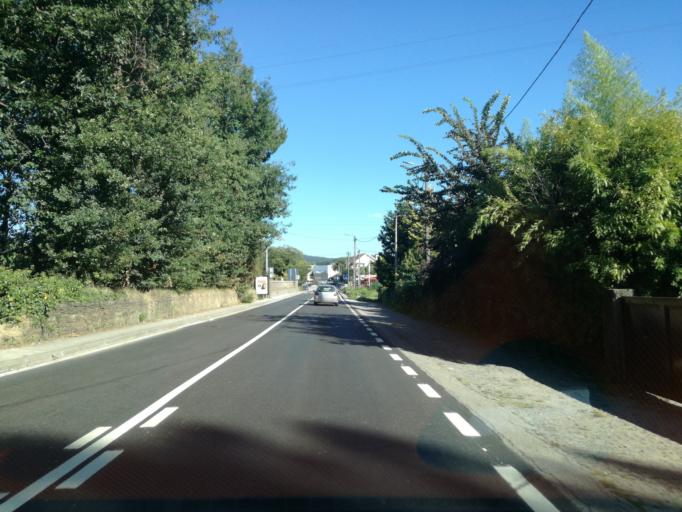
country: PT
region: Porto
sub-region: Valongo
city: Alfena
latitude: 41.2599
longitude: -8.4886
